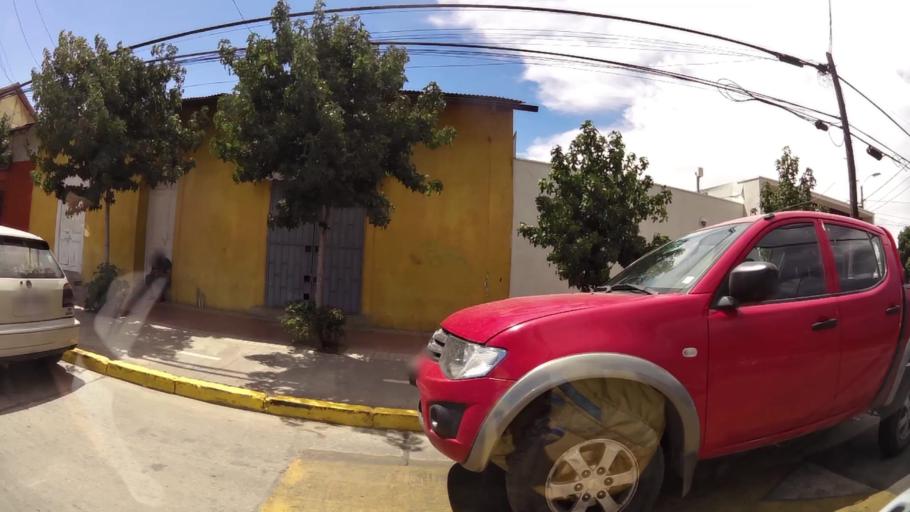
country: CL
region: O'Higgins
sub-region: Provincia de Cachapoal
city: Graneros
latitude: -33.9788
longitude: -70.7123
